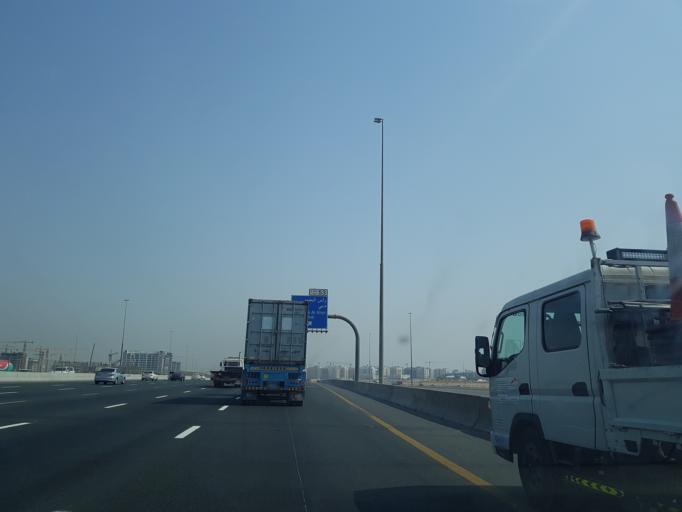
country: AE
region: Ash Shariqah
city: Sharjah
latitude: 25.1803
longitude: 55.3972
